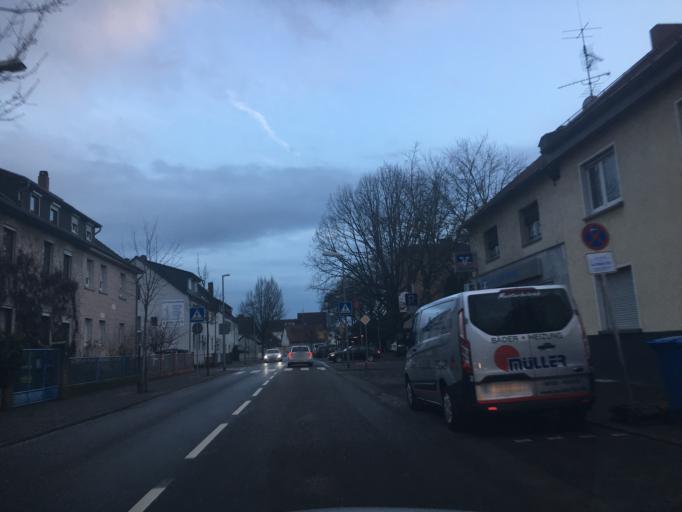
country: DE
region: Hesse
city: Kelsterbach
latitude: 50.0545
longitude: 8.4991
